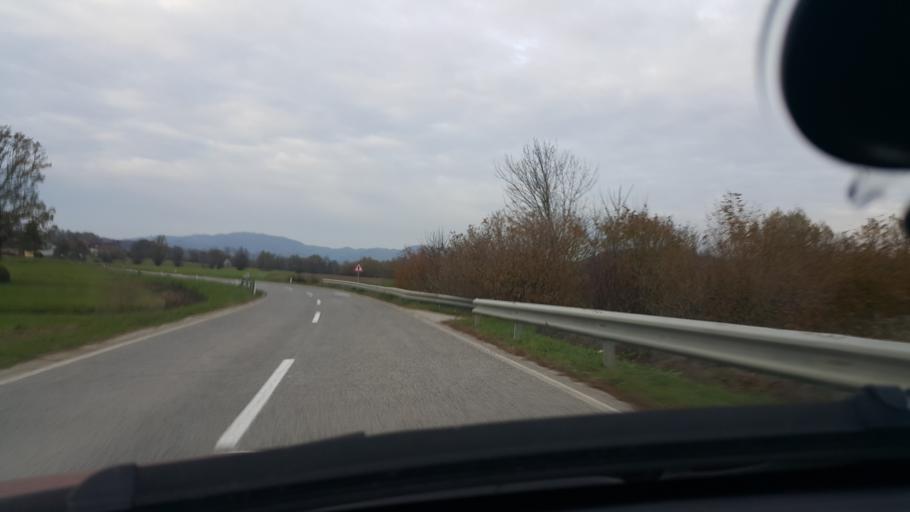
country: SI
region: Bistrica ob Sotli
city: Bistrica ob Sotli
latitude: 46.0810
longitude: 15.6344
